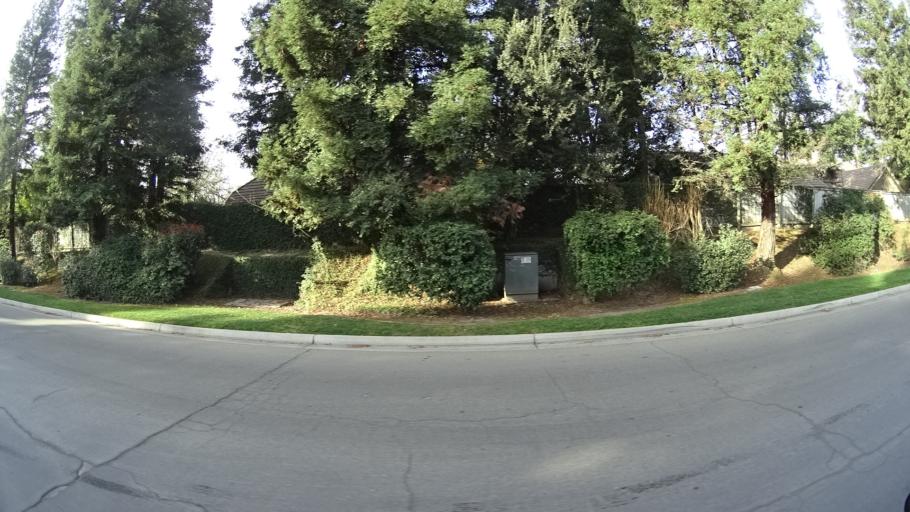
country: US
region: California
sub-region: Fresno County
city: Clovis
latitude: 36.8708
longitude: -119.7733
